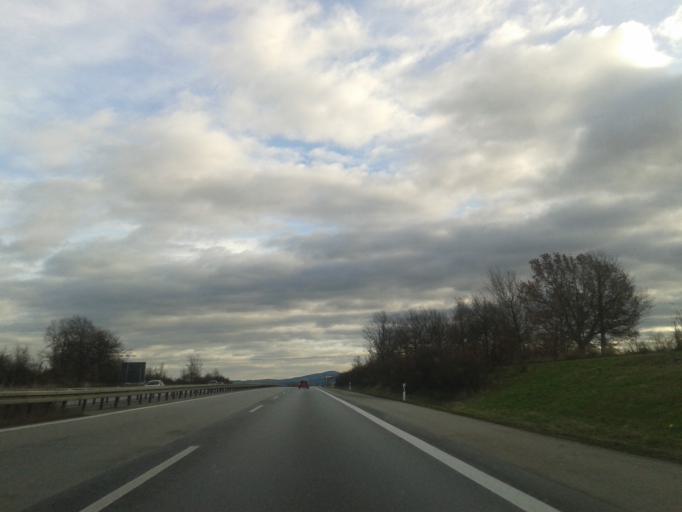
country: DE
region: Saxony
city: Goda
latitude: 51.1905
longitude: 14.3663
